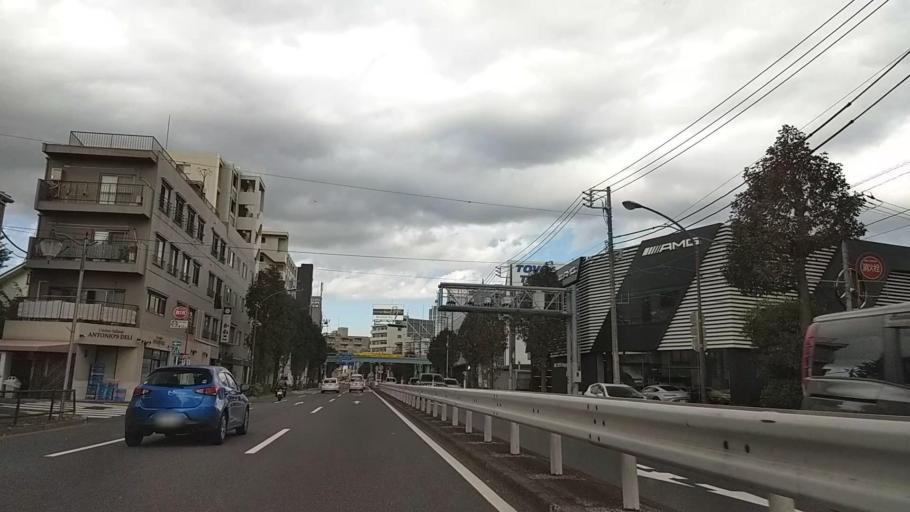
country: JP
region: Tokyo
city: Tokyo
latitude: 35.6167
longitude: 139.6360
